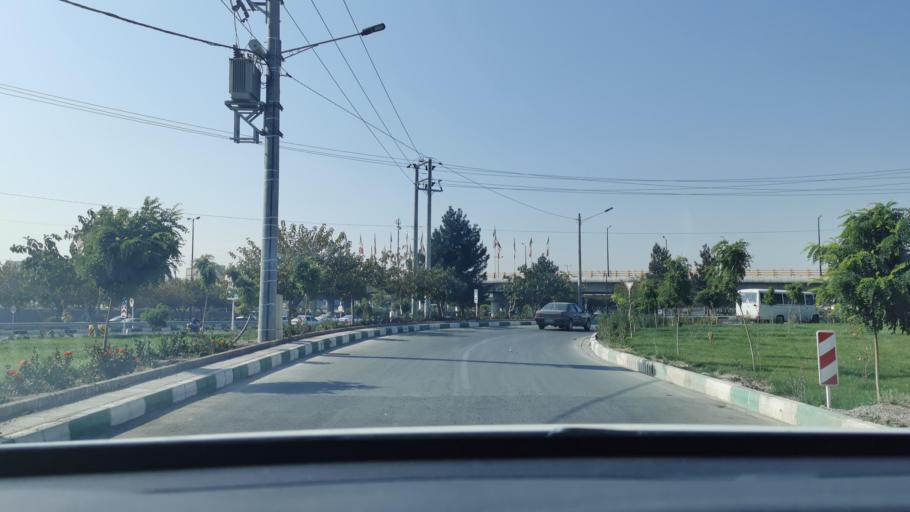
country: IR
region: Razavi Khorasan
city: Mashhad
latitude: 36.3367
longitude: 59.6071
